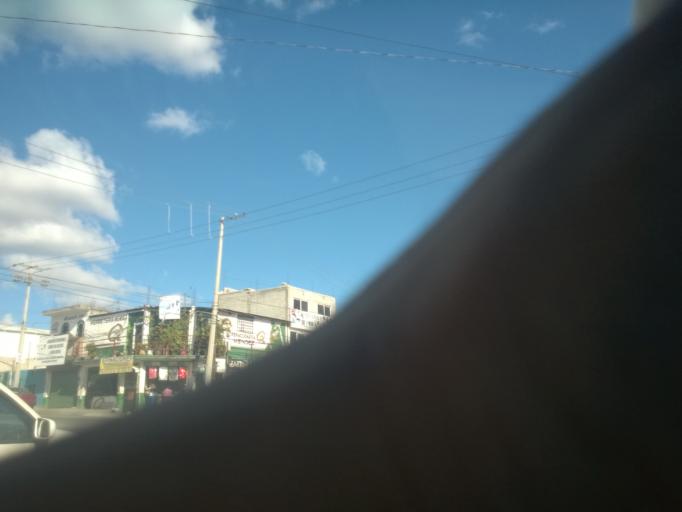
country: MX
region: Guanajuato
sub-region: Leon
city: Ejido la Joya
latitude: 21.1194
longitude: -101.7170
